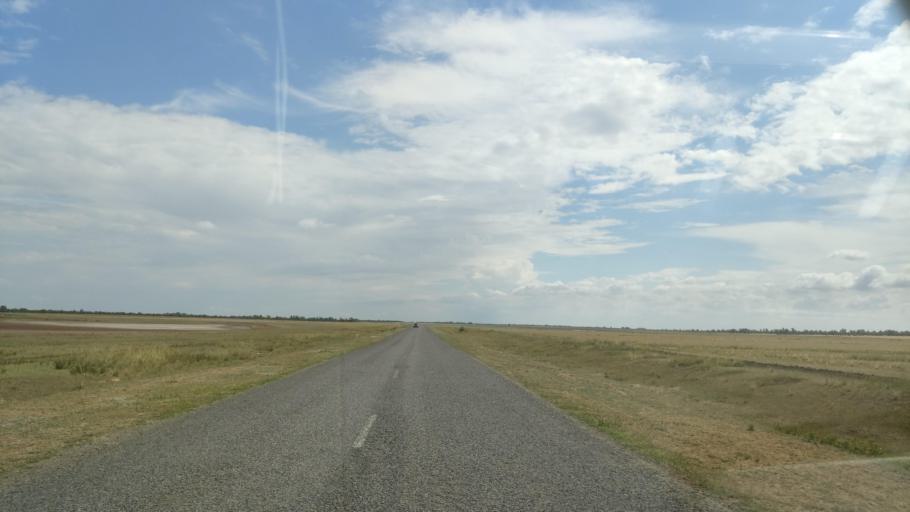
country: KZ
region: Pavlodar
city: Pavlodar
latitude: 52.6351
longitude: 76.9125
